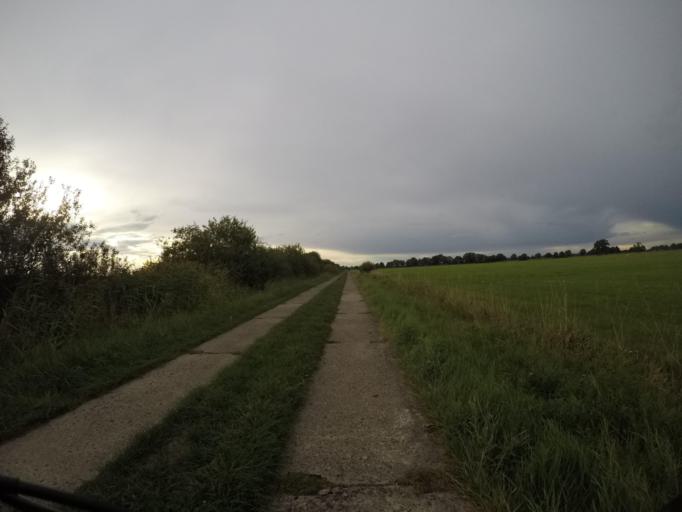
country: DE
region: Lower Saxony
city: Neu Darchau
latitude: 53.2721
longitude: 10.8685
